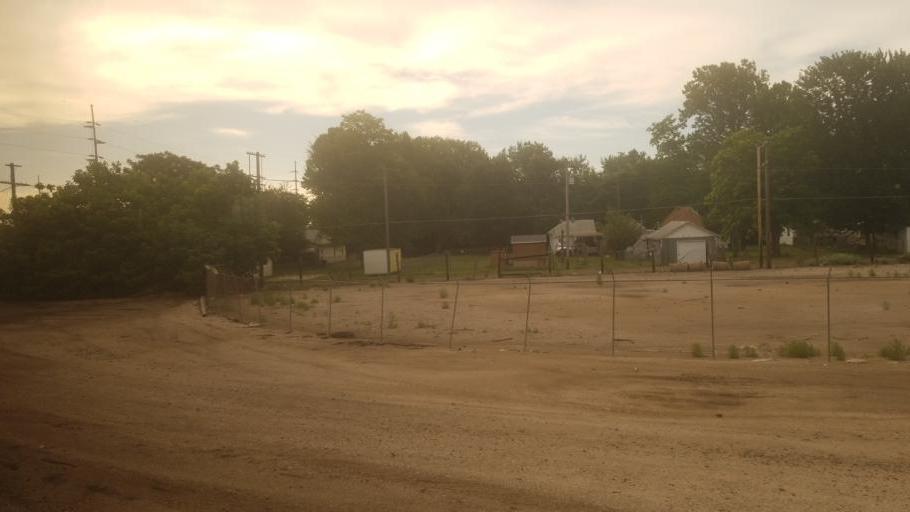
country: US
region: Kansas
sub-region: Shawnee County
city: Topeka
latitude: 39.0544
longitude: -95.6625
